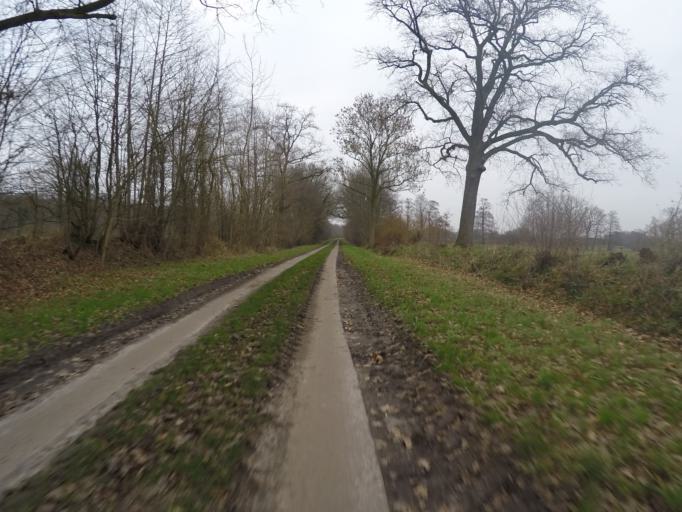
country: DE
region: Schleswig-Holstein
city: Borstel-Hohenraden
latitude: 53.7030
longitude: 9.8396
